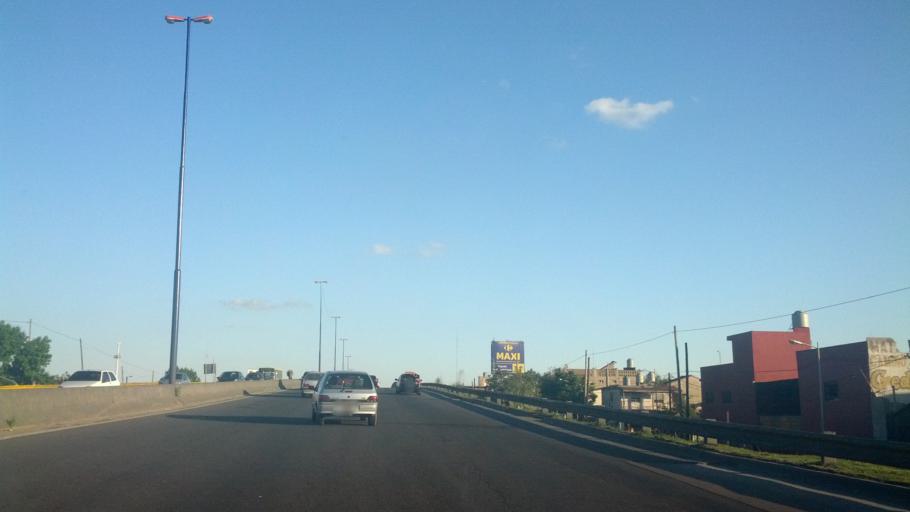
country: AR
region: Buenos Aires F.D.
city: Villa Lugano
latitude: -34.7117
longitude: -58.4540
